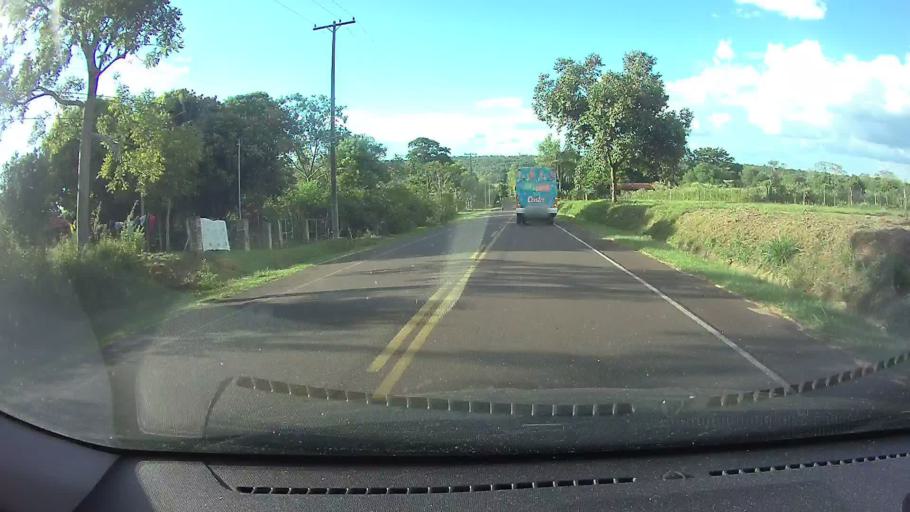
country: PY
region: Cordillera
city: Altos
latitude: -25.1957
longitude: -57.2236
